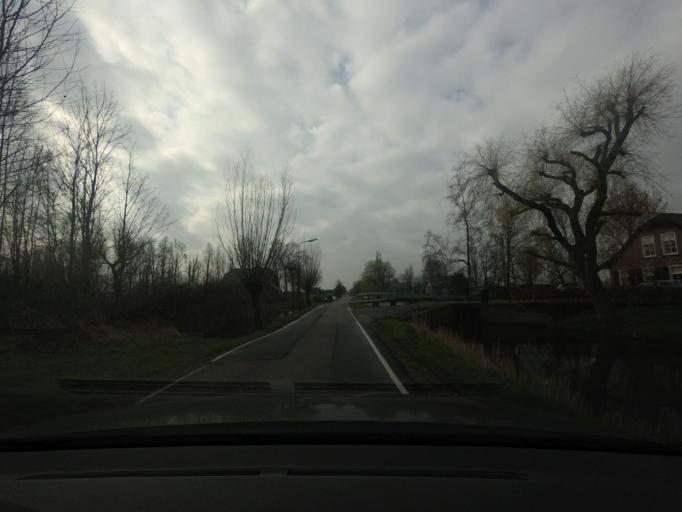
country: NL
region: Utrecht
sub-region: Gemeente De Ronde Venen
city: Mijdrecht
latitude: 52.1579
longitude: 4.8925
